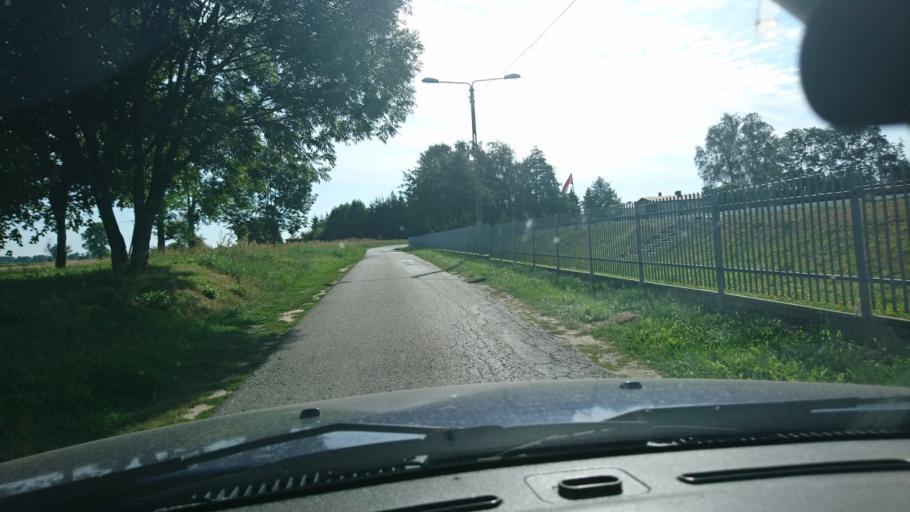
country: PL
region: Greater Poland Voivodeship
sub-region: Powiat ostrowski
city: Odolanow
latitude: 51.5767
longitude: 17.6786
